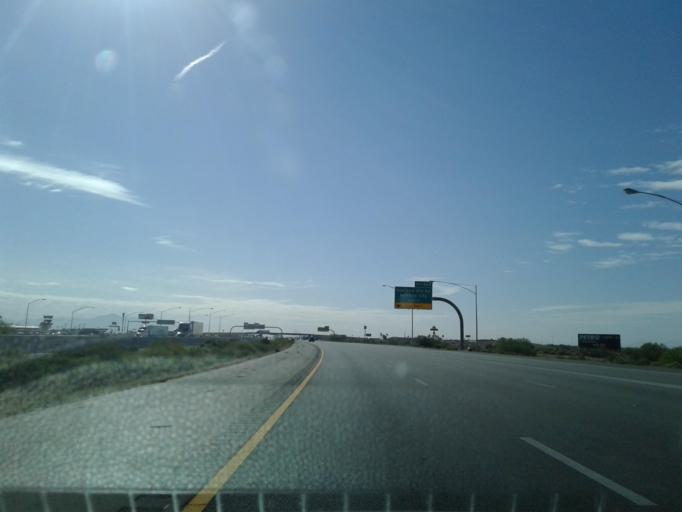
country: US
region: Arizona
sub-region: Pinal County
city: Arizona City
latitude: 32.8140
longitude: -111.6796
